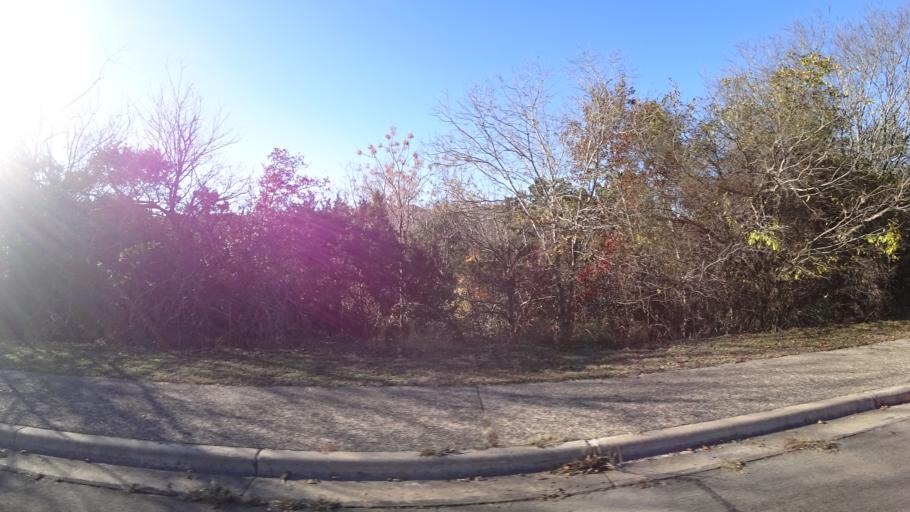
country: US
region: Texas
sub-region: Travis County
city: Wells Branch
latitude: 30.4014
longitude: -97.6958
